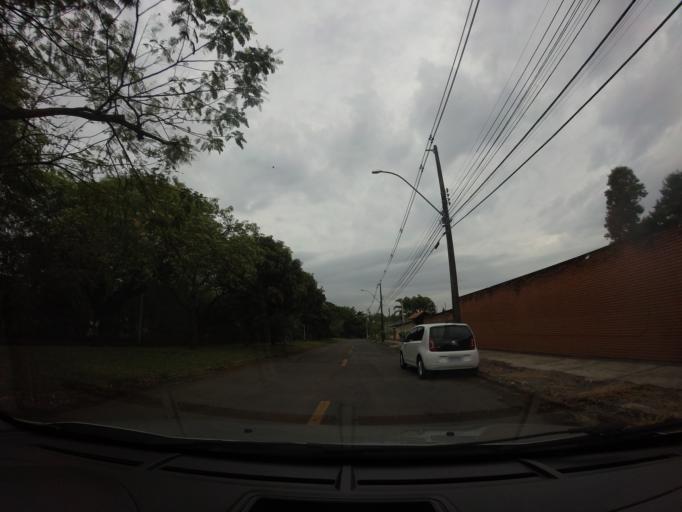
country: BR
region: Sao Paulo
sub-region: Piracicaba
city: Piracicaba
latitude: -22.7556
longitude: -47.5945
